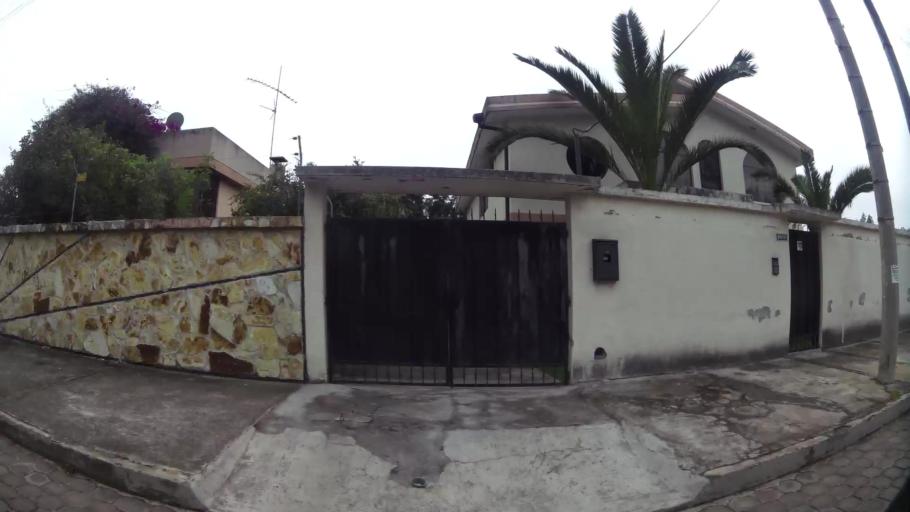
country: EC
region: Pichincha
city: Quito
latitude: -0.2718
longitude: -78.4788
